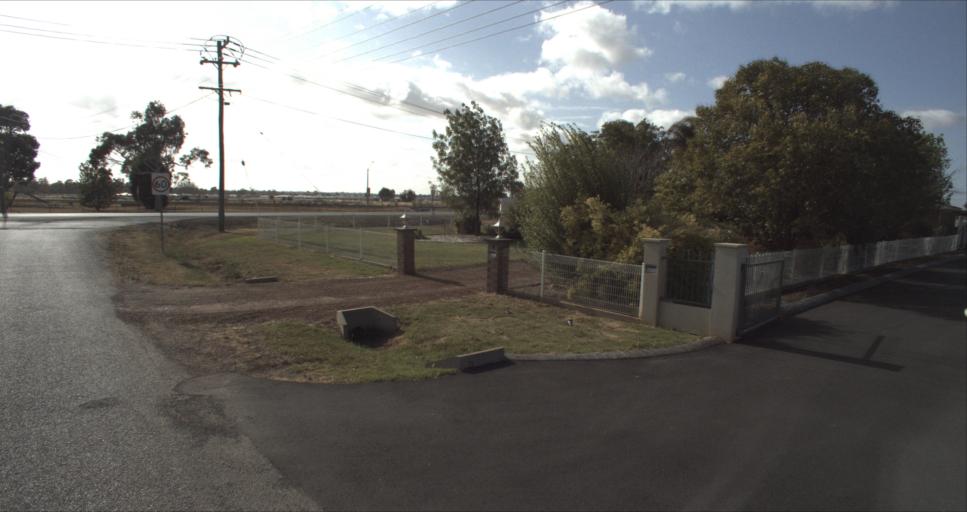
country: AU
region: New South Wales
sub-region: Leeton
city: Leeton
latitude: -34.5682
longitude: 146.3932
